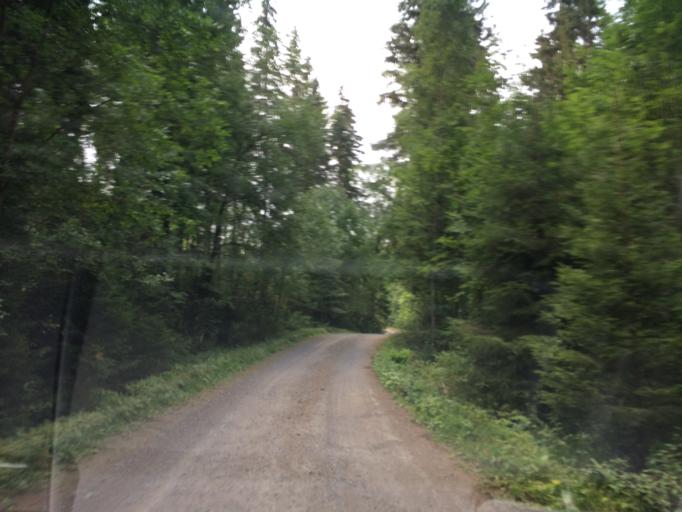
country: FI
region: Haeme
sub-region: Haemeenlinna
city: Hauho
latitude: 61.0738
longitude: 24.6504
